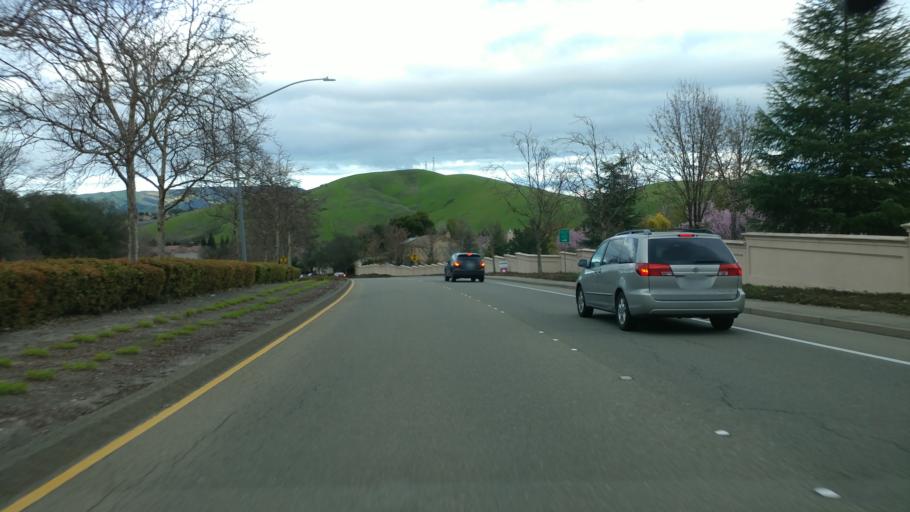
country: US
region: California
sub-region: Contra Costa County
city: Blackhawk
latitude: 37.7879
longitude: -121.9294
